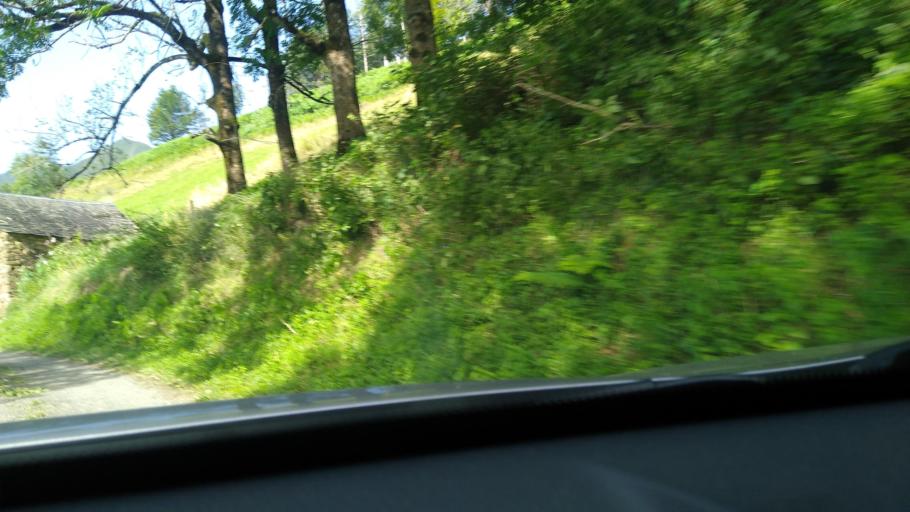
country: FR
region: Midi-Pyrenees
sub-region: Departement de l'Ariege
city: Saint-Girons
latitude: 42.7932
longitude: 1.1656
